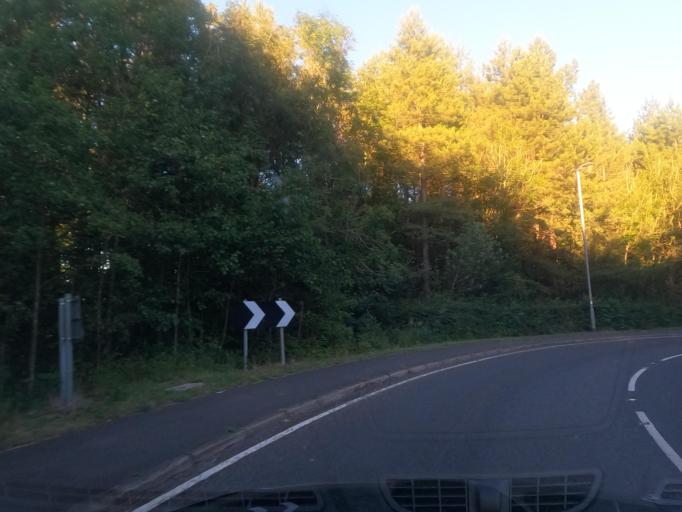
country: GB
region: England
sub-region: Northumberland
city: Seghill
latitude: 55.0800
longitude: -1.5492
